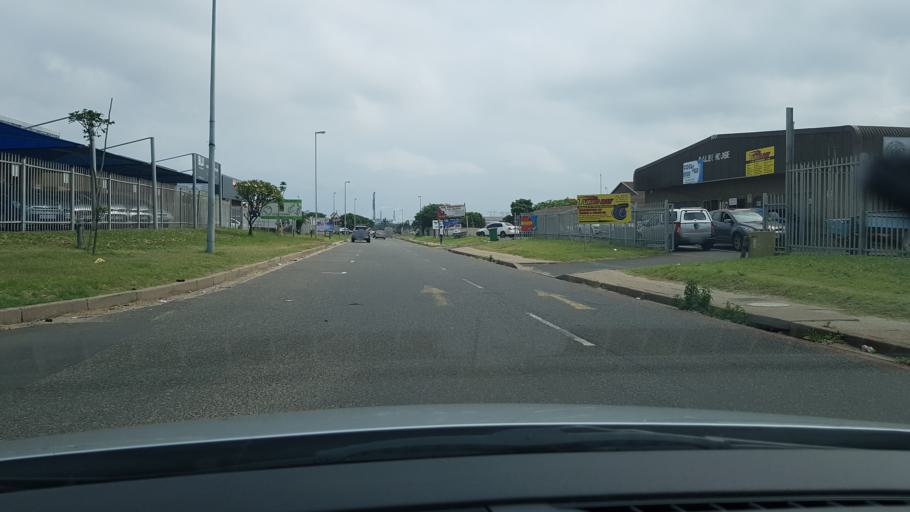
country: ZA
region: KwaZulu-Natal
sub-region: uThungulu District Municipality
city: Richards Bay
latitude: -28.7549
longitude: 32.0439
